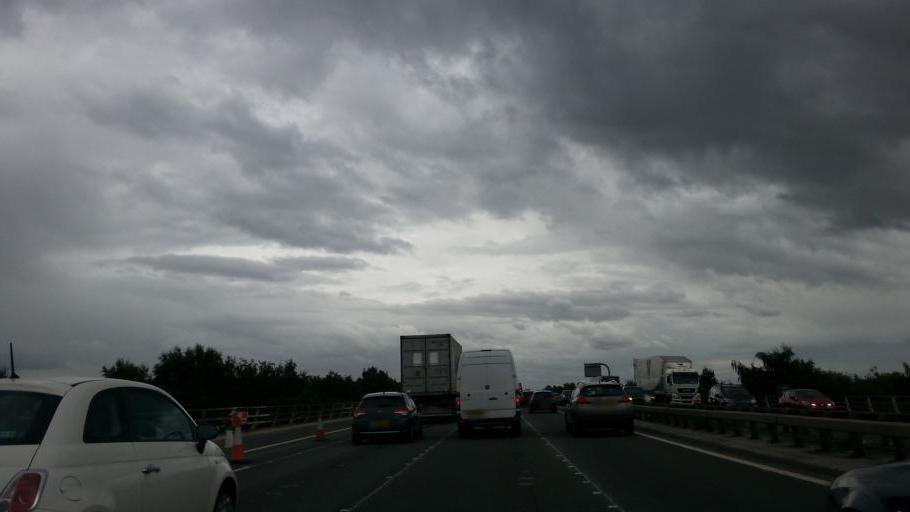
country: GB
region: England
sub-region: City and Borough of Wakefield
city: Normanton
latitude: 53.7219
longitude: -1.4285
